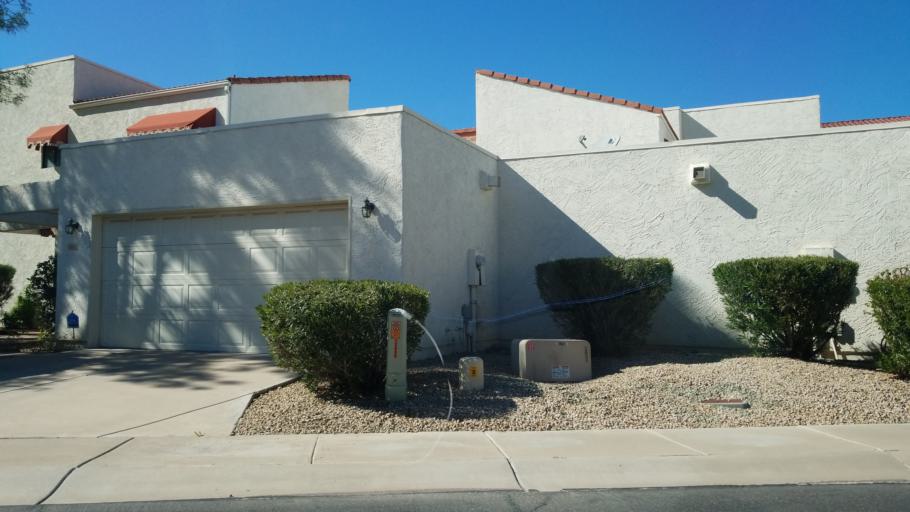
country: US
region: Arizona
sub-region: Maricopa County
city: Paradise Valley
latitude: 33.6124
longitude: -111.9906
